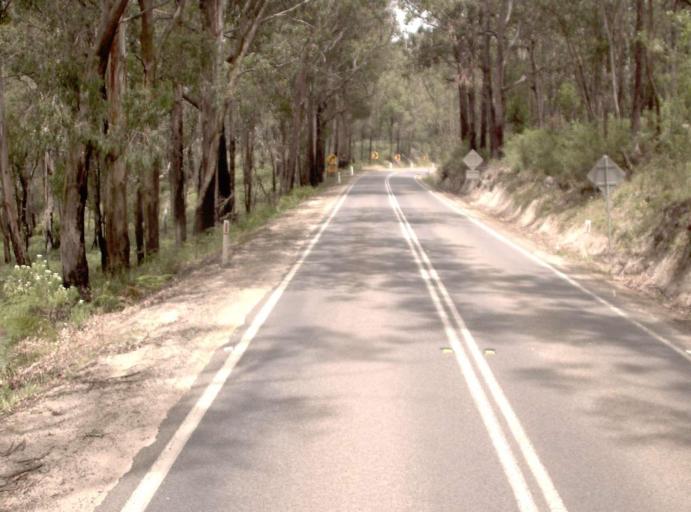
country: AU
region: Victoria
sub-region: Latrobe
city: Traralgon
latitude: -38.4202
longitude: 146.7477
